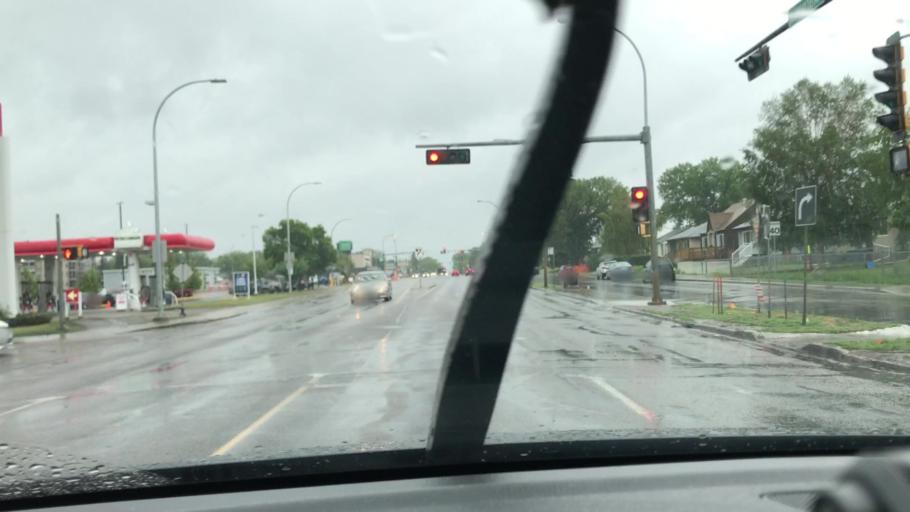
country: CA
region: Alberta
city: Edmonton
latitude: 53.5180
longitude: -113.4586
